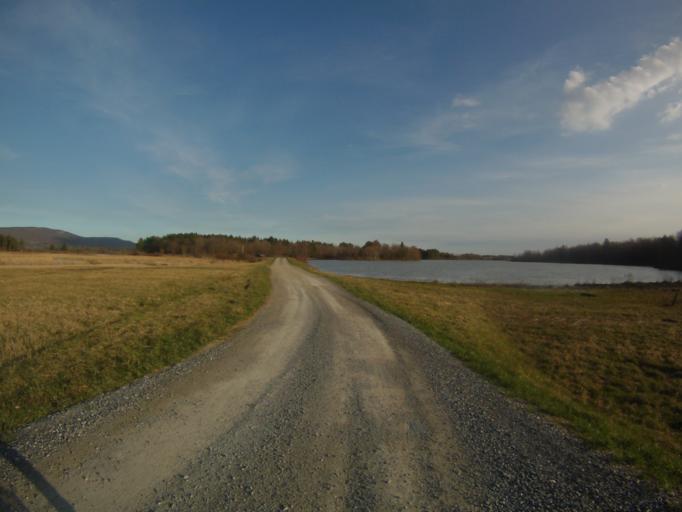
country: US
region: New York
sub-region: Essex County
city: Port Henry
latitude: 44.0750
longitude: -73.3507
